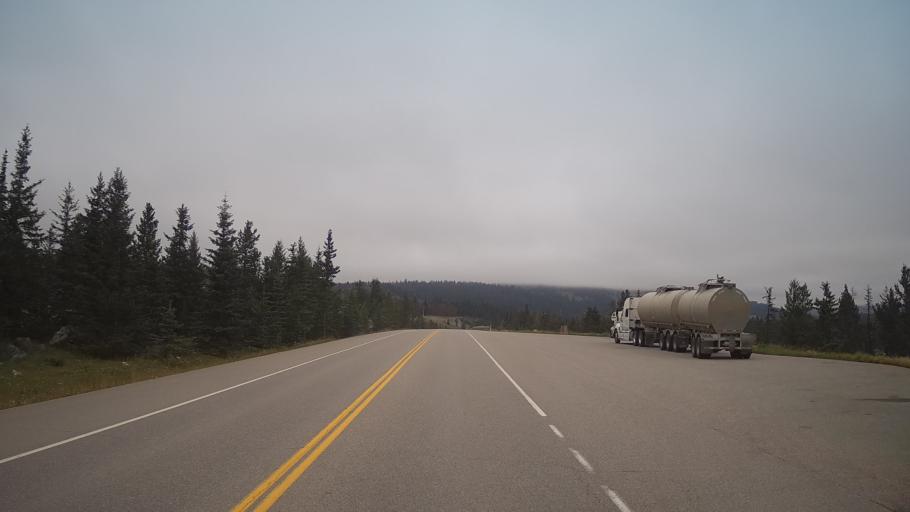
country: CA
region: Alberta
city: Jasper Park Lodge
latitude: 52.8759
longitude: -118.0714
